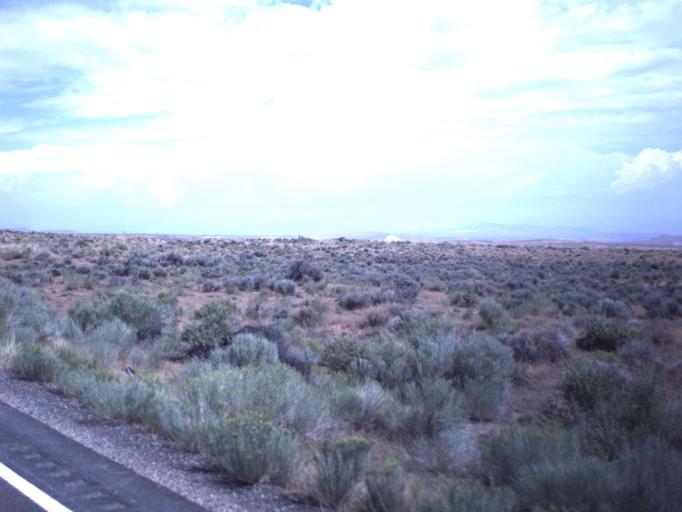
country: US
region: Utah
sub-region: Uintah County
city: Naples
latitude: 40.2507
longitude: -109.4260
